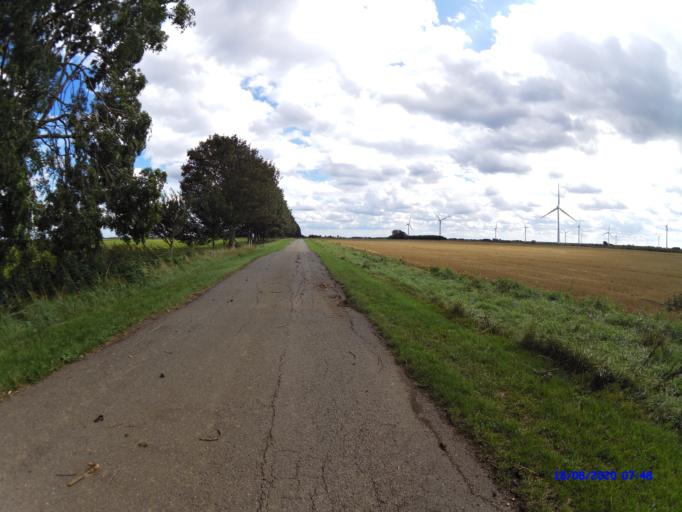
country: GB
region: England
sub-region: Cambridgeshire
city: Whittlesey
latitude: 52.5227
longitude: -0.0978
